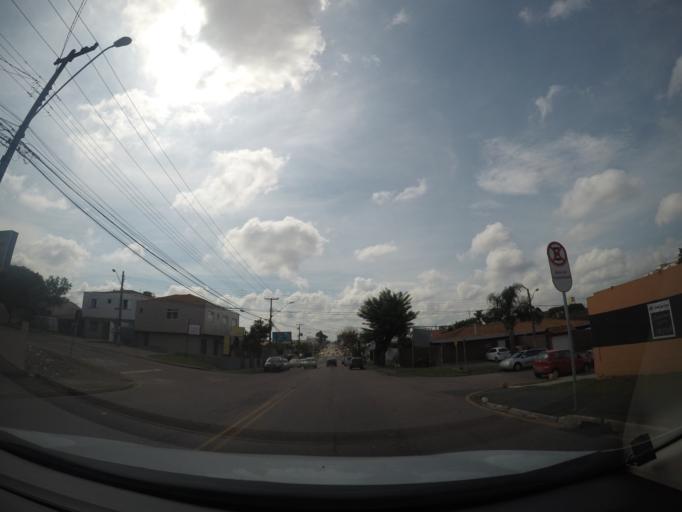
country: BR
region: Parana
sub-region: Curitiba
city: Curitiba
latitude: -25.4909
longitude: -49.2768
